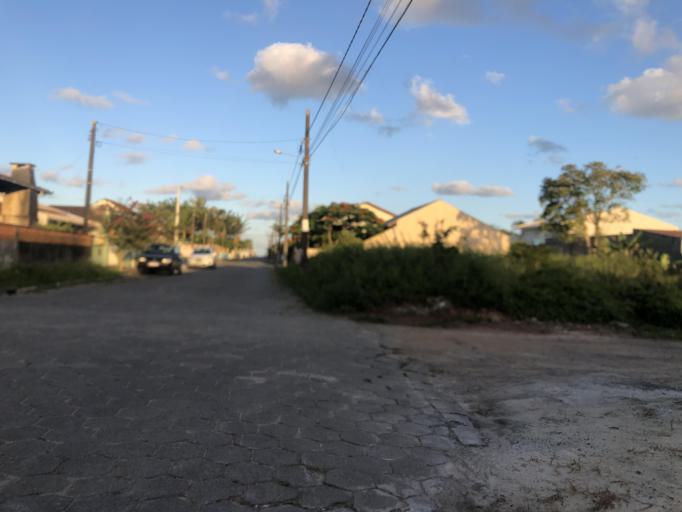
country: BR
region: Santa Catarina
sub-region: Sao Francisco Do Sul
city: Sao Francisco do Sul
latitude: -26.2196
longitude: -48.5275
